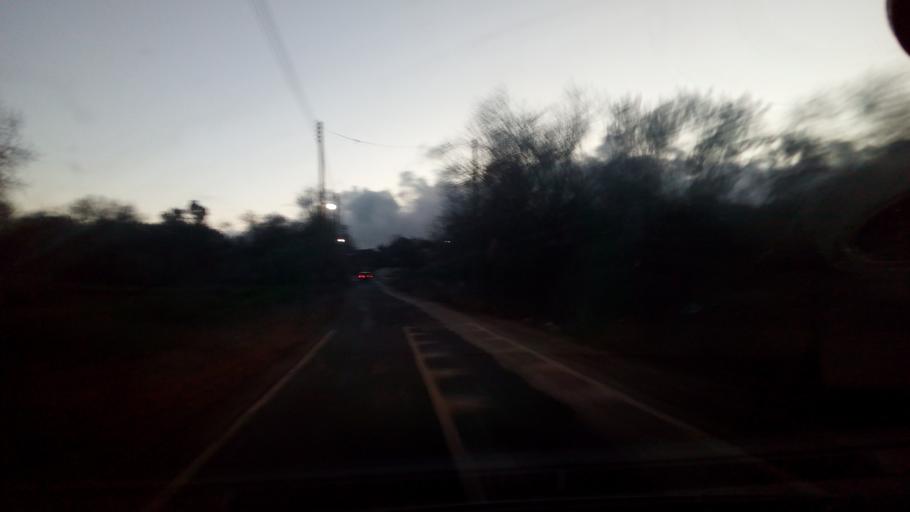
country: CY
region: Pafos
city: Mesogi
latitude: 34.8824
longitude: 32.5064
